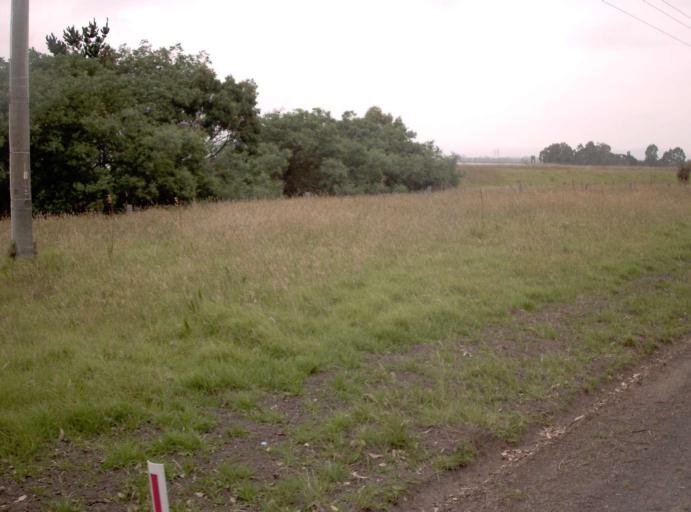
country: AU
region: Victoria
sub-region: Latrobe
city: Morwell
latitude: -38.2886
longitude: 146.3652
